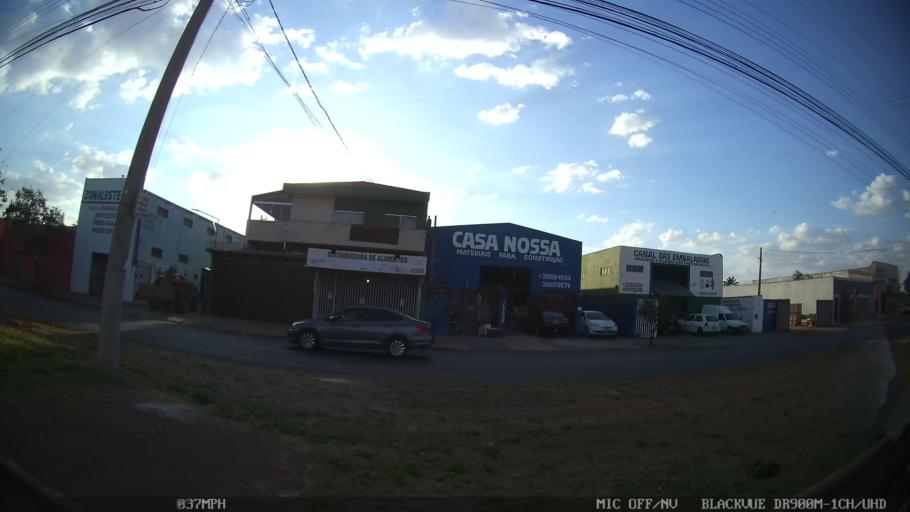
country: BR
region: Sao Paulo
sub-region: Ribeirao Preto
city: Ribeirao Preto
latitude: -21.1644
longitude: -47.7455
